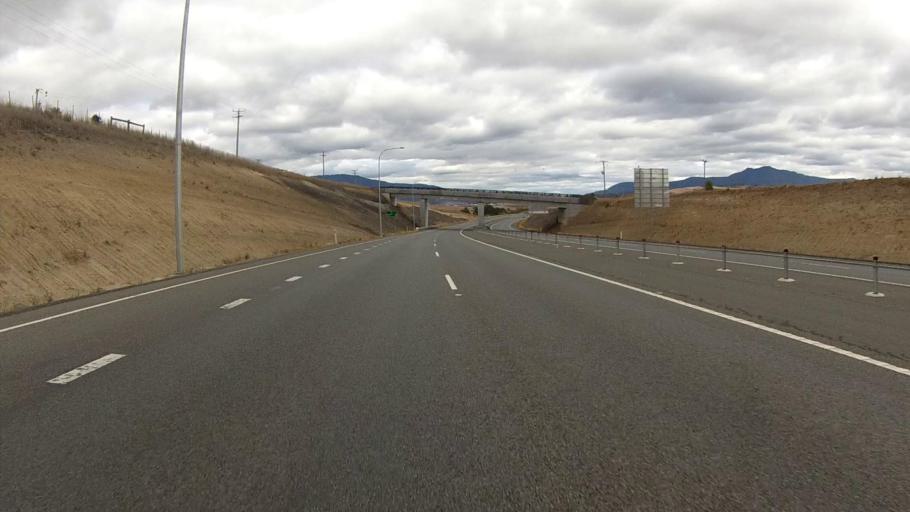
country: AU
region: Tasmania
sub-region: Brighton
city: Bridgewater
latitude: -42.7023
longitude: 147.2727
